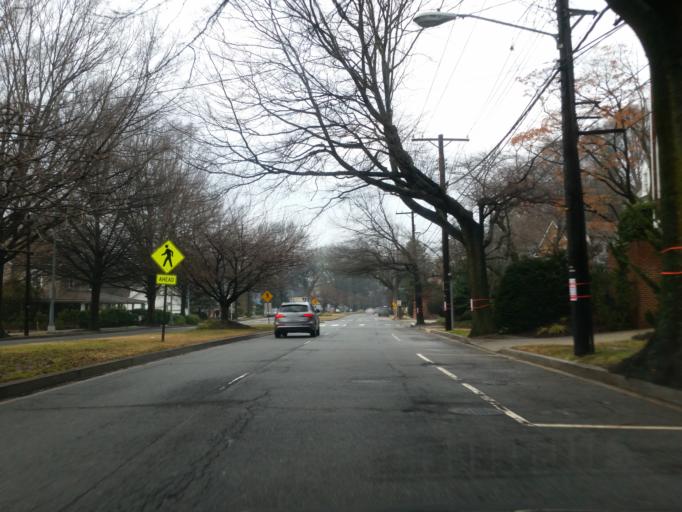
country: US
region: Maryland
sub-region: Montgomery County
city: Brookmont
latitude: 38.9321
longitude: -77.1083
